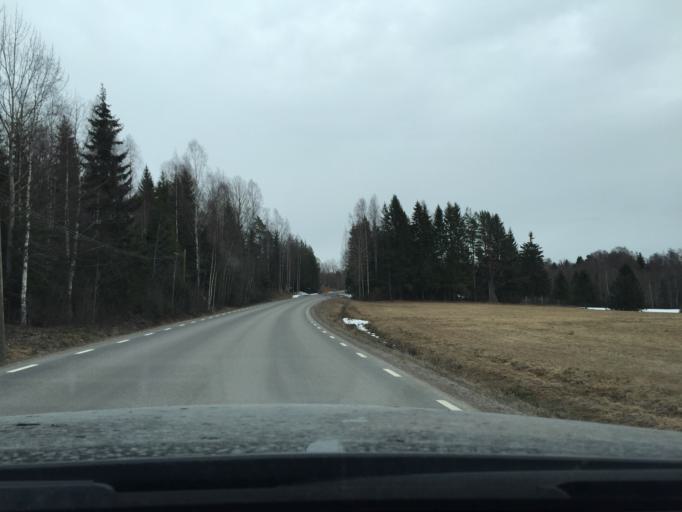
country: SE
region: Gaevleborg
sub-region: Sandvikens Kommun
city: Jarbo
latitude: 60.7625
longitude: 16.5228
